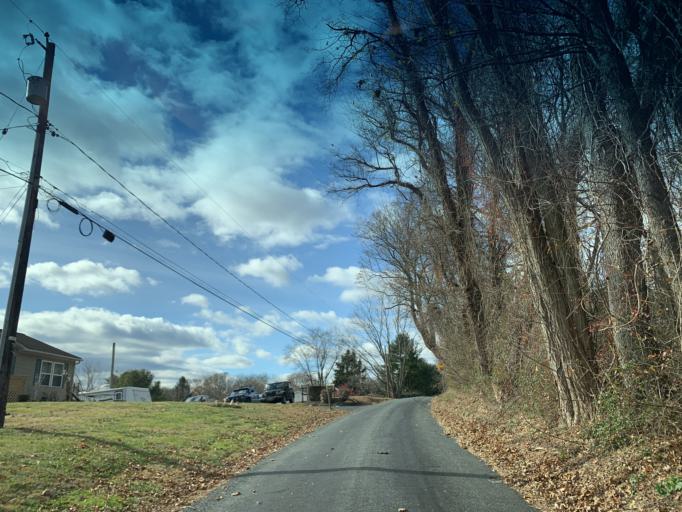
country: US
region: Maryland
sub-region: Harford County
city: Jarrettsville
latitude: 39.5949
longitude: -76.4187
